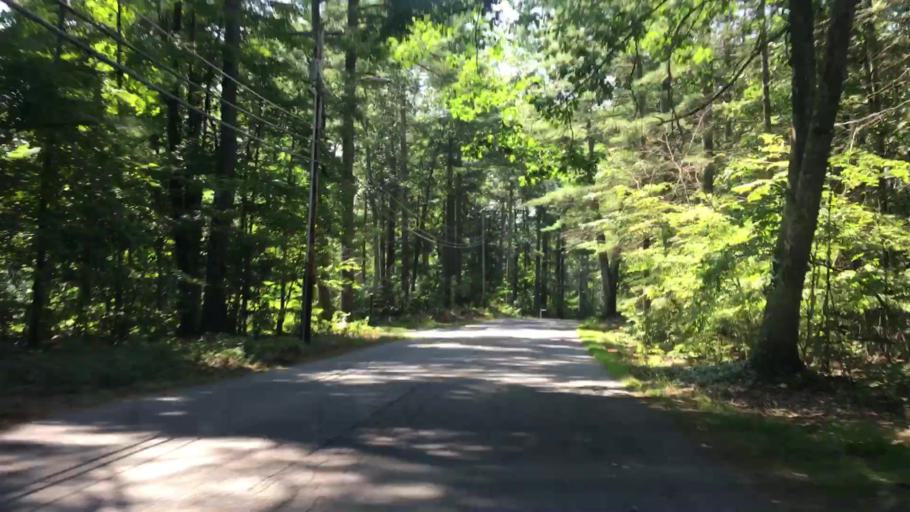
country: US
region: New Hampshire
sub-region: Rockingham County
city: Hampstead
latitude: 42.8710
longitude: -71.2217
